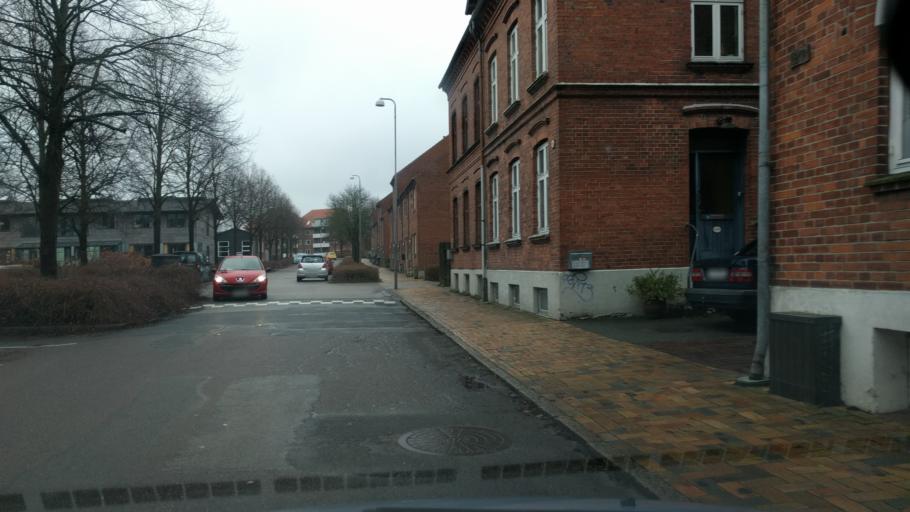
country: DK
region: South Denmark
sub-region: Odense Kommune
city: Odense
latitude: 55.4004
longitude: 10.4000
